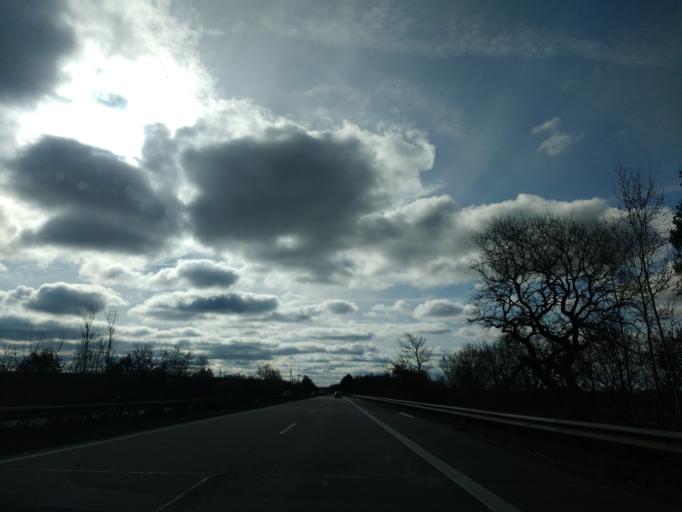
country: DE
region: Lower Saxony
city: Midlum
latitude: 53.6638
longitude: 8.6587
